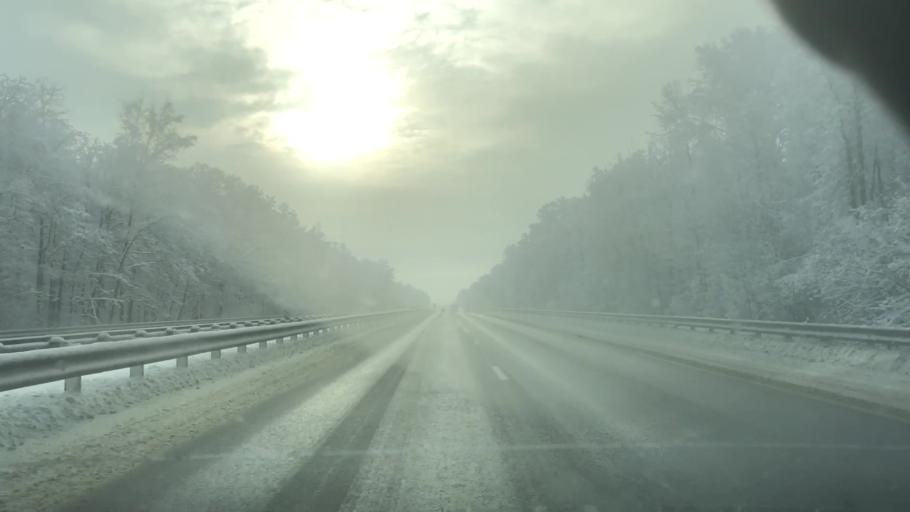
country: RU
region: Tula
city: Venev
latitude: 54.3675
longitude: 38.1547
